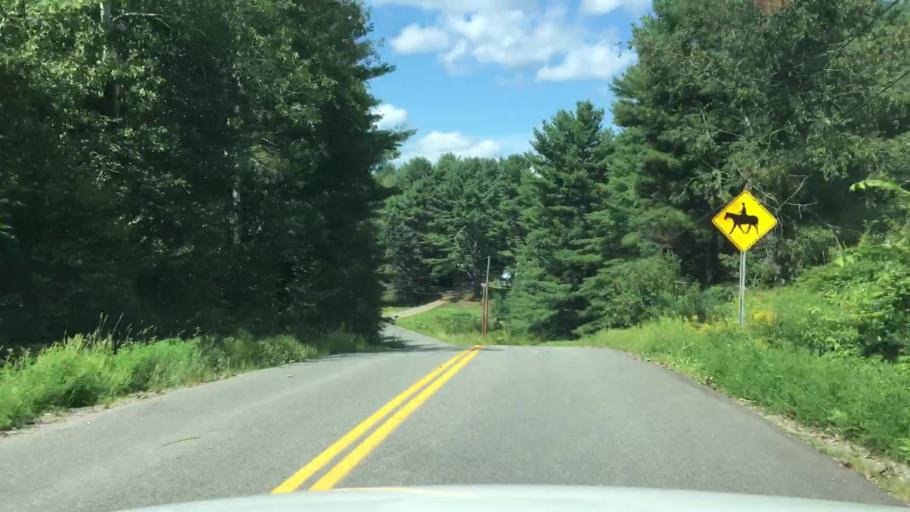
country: US
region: Maine
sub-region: Kennebec County
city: Manchester
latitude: 44.3549
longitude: -69.8174
